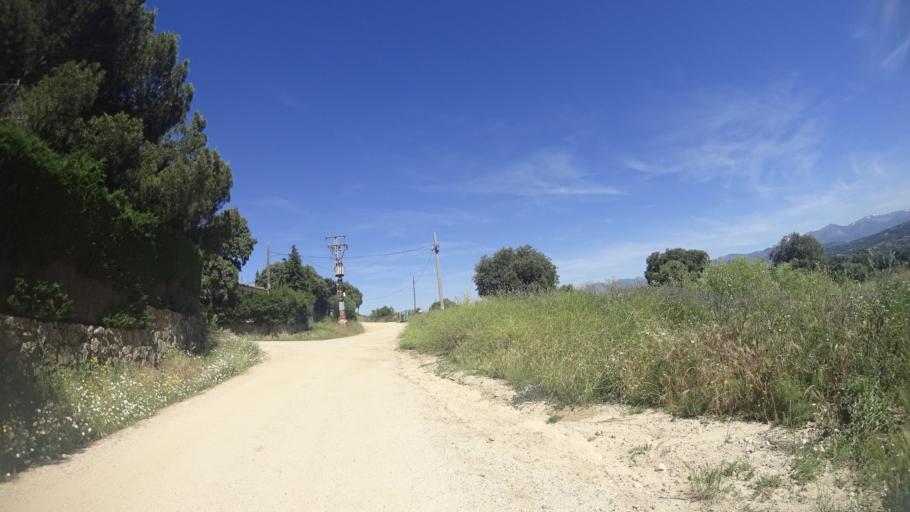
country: ES
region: Madrid
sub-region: Provincia de Madrid
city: Galapagar
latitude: 40.5973
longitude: -3.9977
